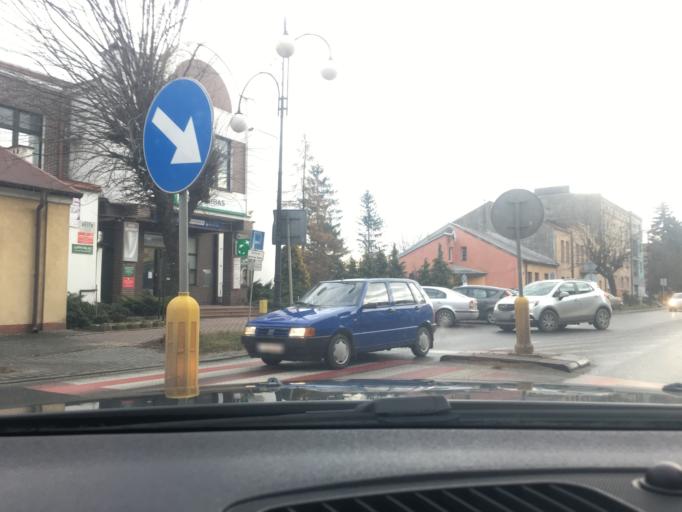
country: PL
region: Swietokrzyskie
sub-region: Powiat jedrzejowski
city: Jedrzejow
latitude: 50.6457
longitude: 20.2943
